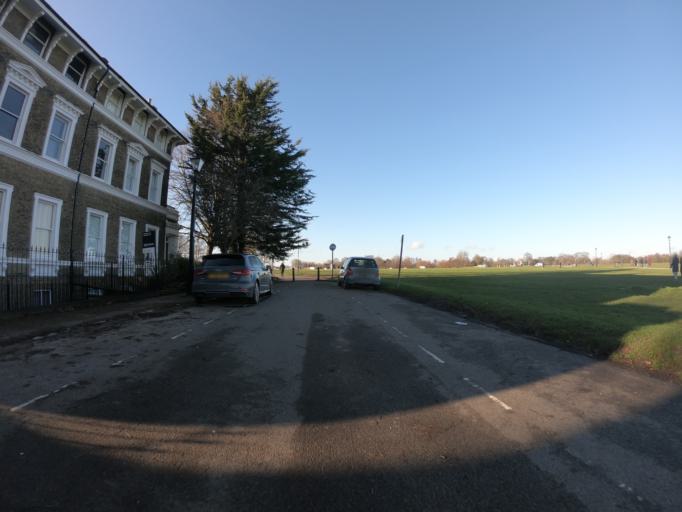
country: GB
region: England
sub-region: Greater London
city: Blackheath
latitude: 51.4700
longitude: 0.0052
